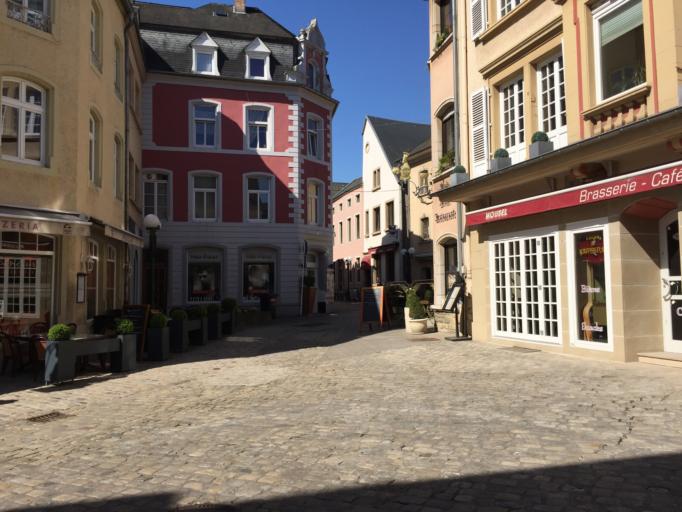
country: LU
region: Grevenmacher
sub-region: Canton d'Echternach
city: Echternach
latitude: 49.8130
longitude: 6.4196
